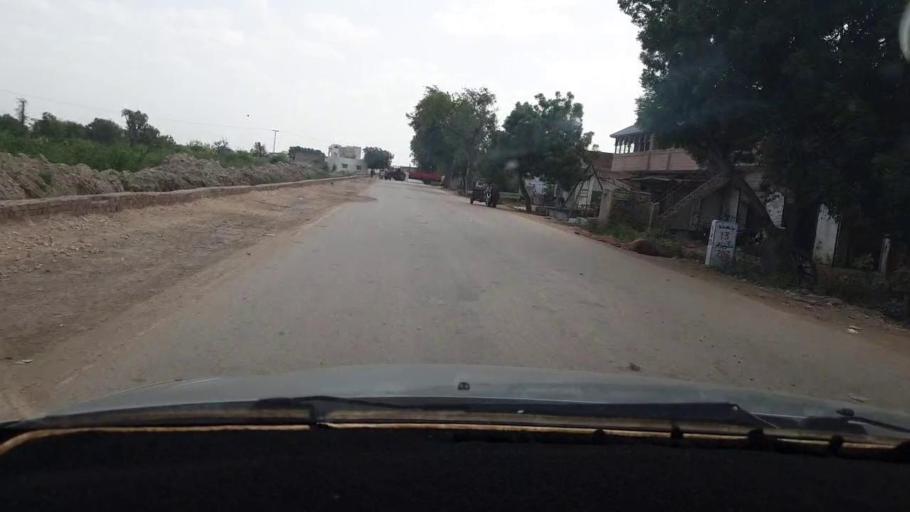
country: PK
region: Sindh
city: Digri
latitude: 25.0646
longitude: 69.2178
